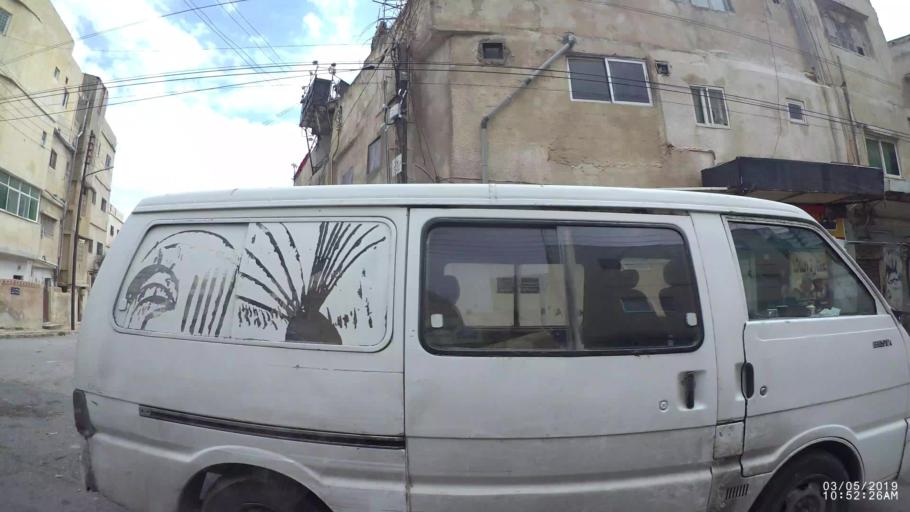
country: JO
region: Amman
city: Amman
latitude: 31.9824
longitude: 35.9206
